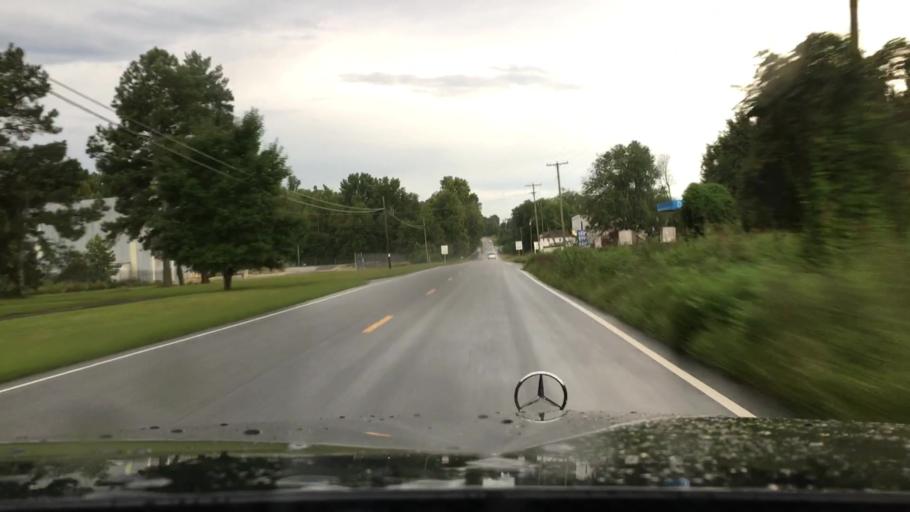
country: US
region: Virginia
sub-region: Amherst County
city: Amherst
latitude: 37.7055
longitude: -79.0251
